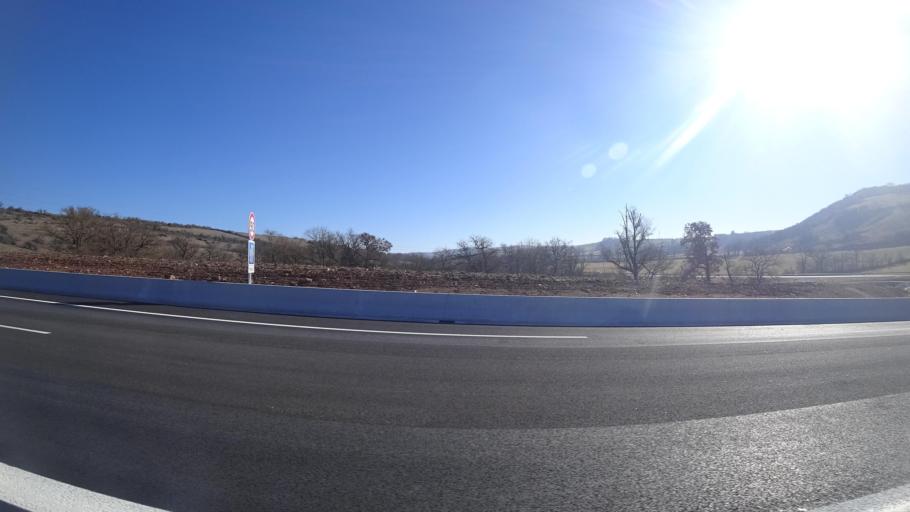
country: FR
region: Midi-Pyrenees
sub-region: Departement de l'Aveyron
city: Sebazac-Concoures
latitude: 44.3763
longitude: 2.6137
